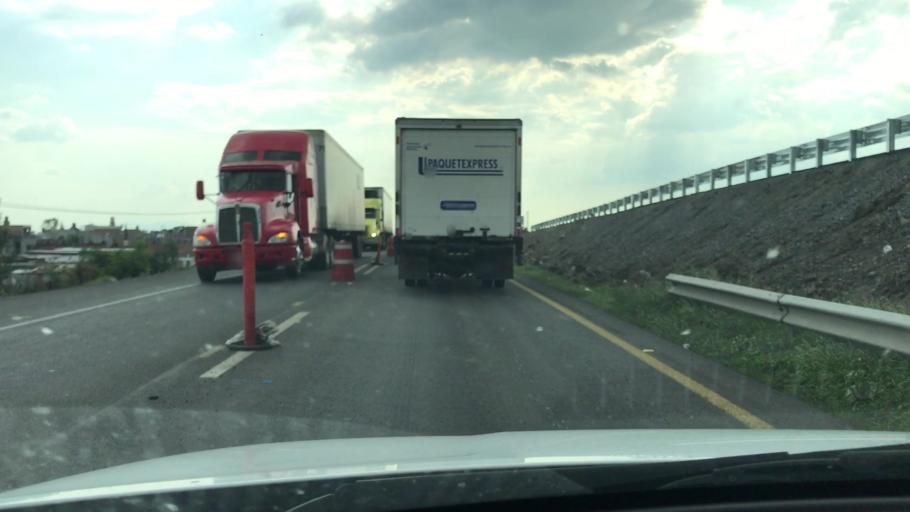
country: MX
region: Guanajuato
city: Irapuato
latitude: 20.6507
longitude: -101.3346
